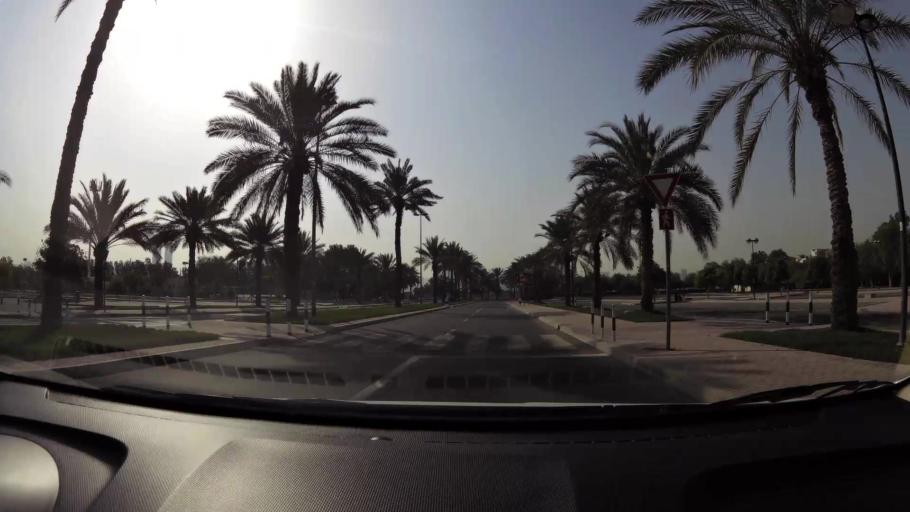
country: AE
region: Ash Shariqah
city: Sharjah
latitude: 25.3164
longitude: 55.3471
